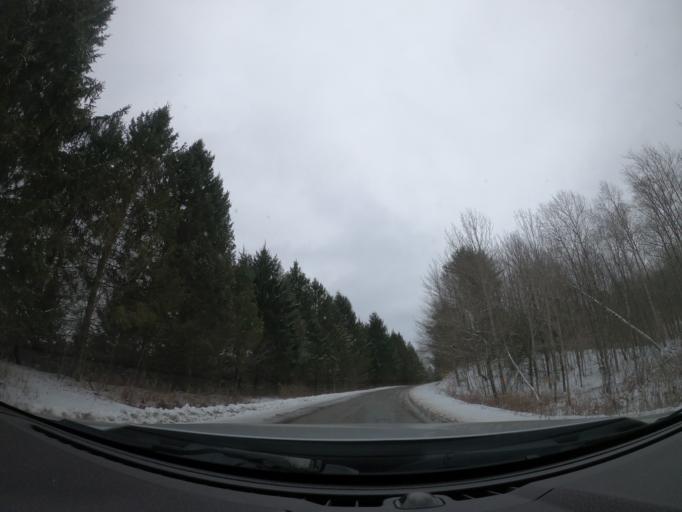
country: US
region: New York
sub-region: Cayuga County
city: Moravia
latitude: 42.7341
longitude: -76.2935
